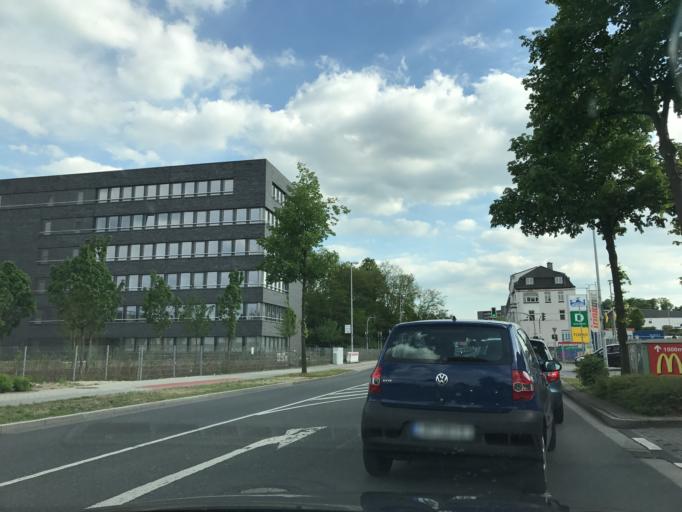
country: DE
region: North Rhine-Westphalia
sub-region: Regierungsbezirk Dusseldorf
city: Muelheim (Ruhr)
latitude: 51.4111
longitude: 6.8687
